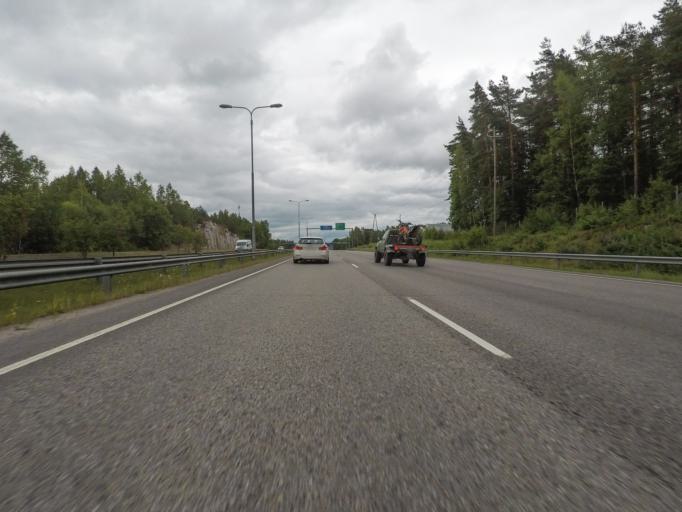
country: FI
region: Varsinais-Suomi
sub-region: Turku
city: Turku
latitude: 60.4977
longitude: 22.2700
